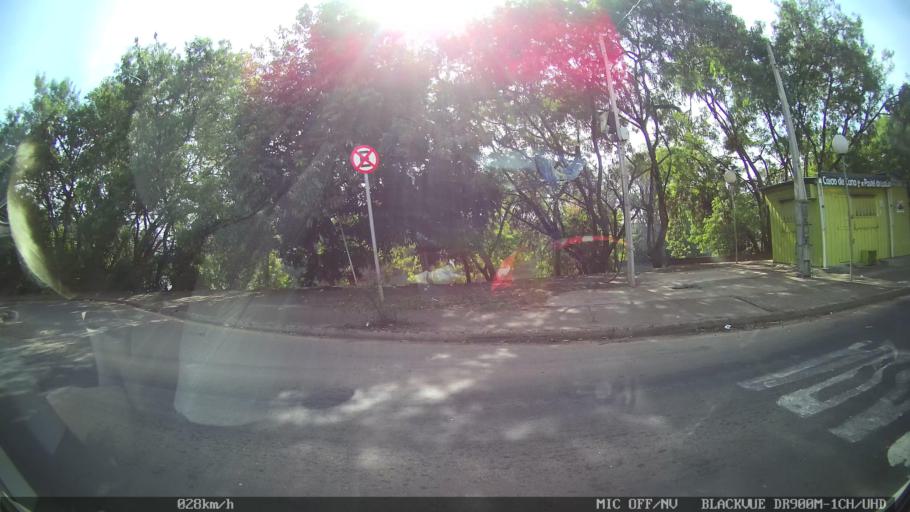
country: BR
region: Sao Paulo
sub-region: Piracicaba
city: Piracicaba
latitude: -22.7192
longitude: -47.6758
